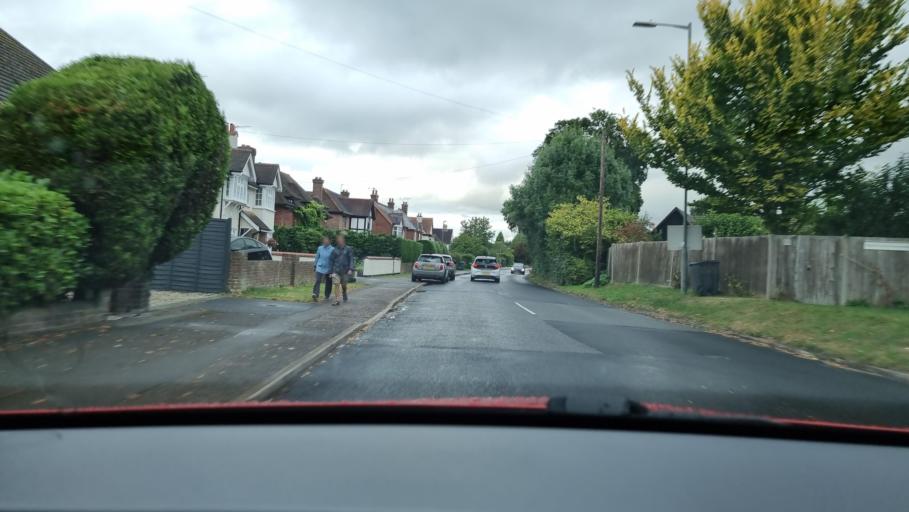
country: GB
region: England
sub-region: Buckinghamshire
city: Chesham
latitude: 51.7097
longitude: -0.5995
